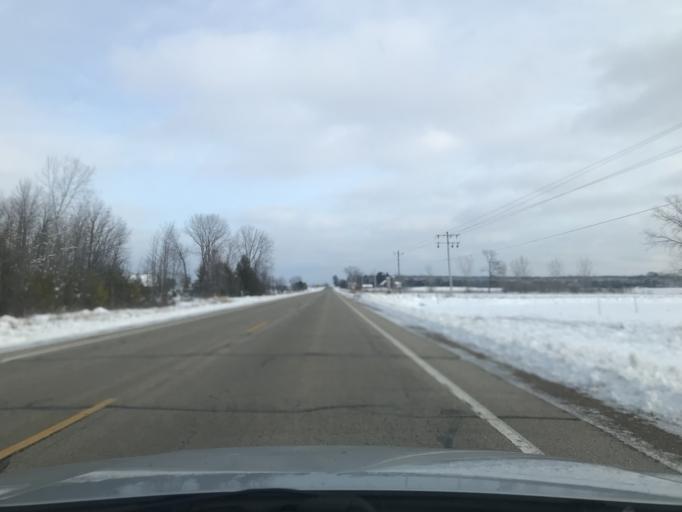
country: US
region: Wisconsin
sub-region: Oconto County
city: Oconto
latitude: 44.8927
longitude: -87.9560
